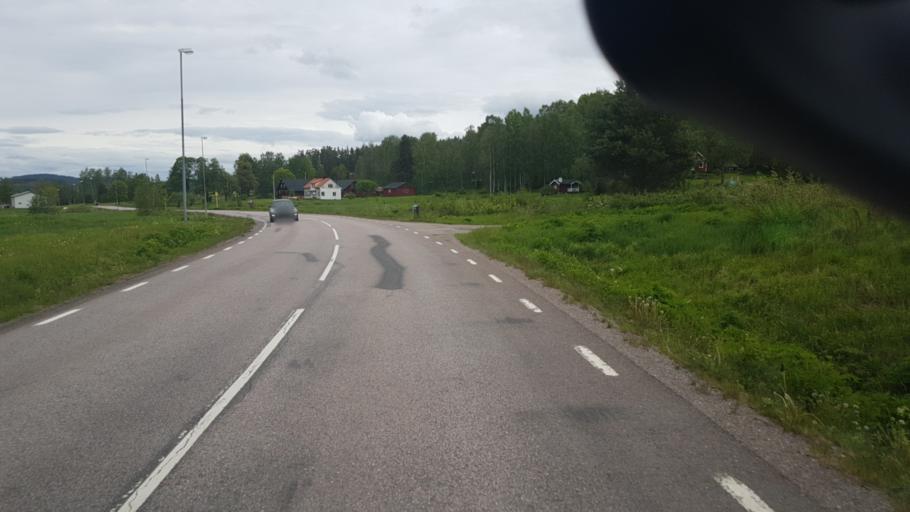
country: SE
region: Vaermland
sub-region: Arvika Kommun
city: Arvika
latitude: 59.7725
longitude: 12.6158
